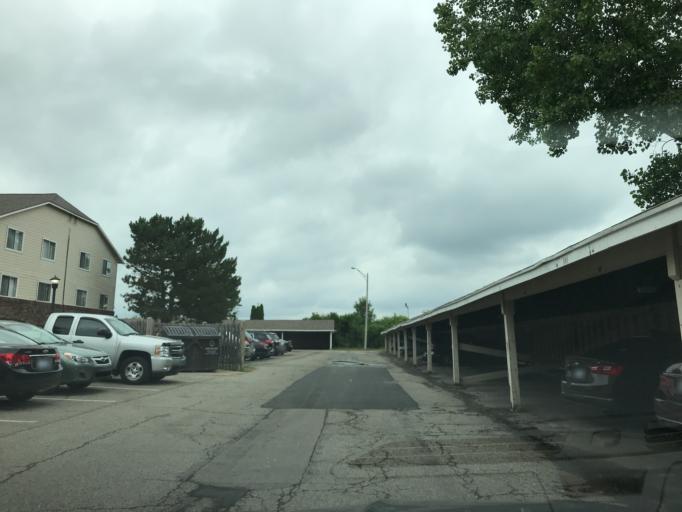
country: US
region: Michigan
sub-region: Eaton County
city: Waverly
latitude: 42.7392
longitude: -84.6651
